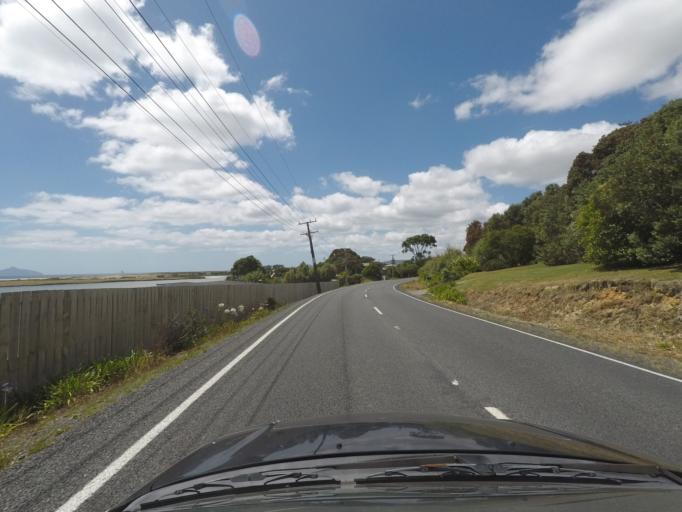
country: NZ
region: Northland
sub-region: Whangarei
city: Ruakaka
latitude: -35.9936
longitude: 174.4702
